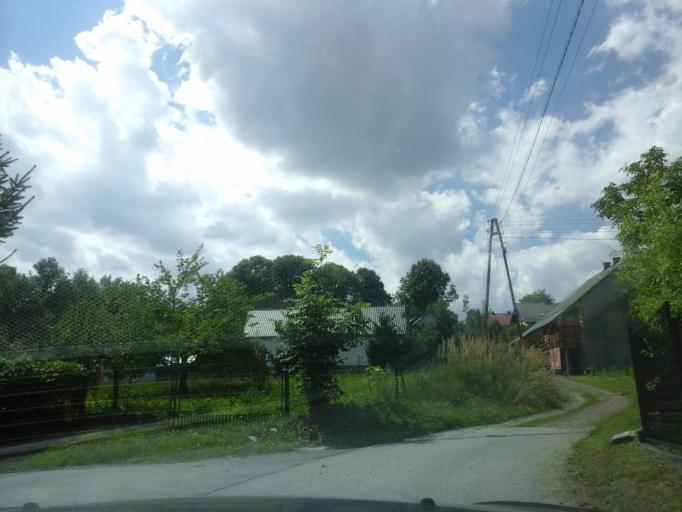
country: PL
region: Lesser Poland Voivodeship
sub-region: Powiat wadowicki
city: Ryczow
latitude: 49.9792
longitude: 19.5452
